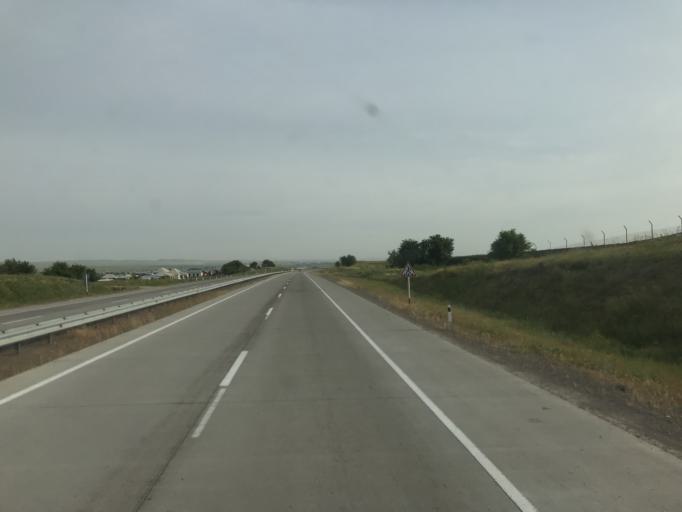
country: KZ
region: Ongtustik Qazaqstan
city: Qazyqurt
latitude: 41.6724
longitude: 69.3943
